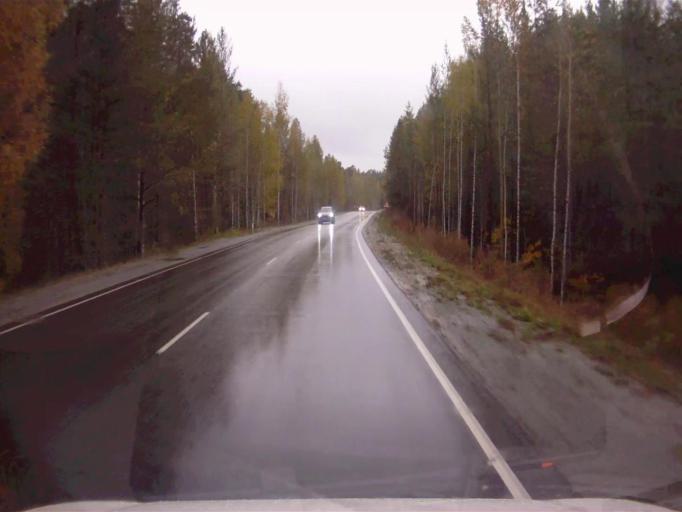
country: RU
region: Chelyabinsk
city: Kyshtym
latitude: 55.6532
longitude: 60.5766
